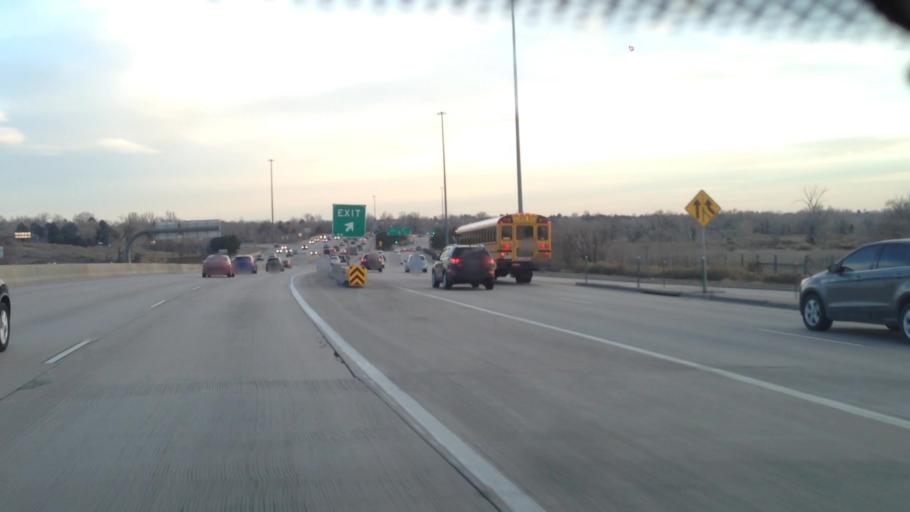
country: US
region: Colorado
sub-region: Adams County
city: Aurora
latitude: 39.6559
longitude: -104.8349
